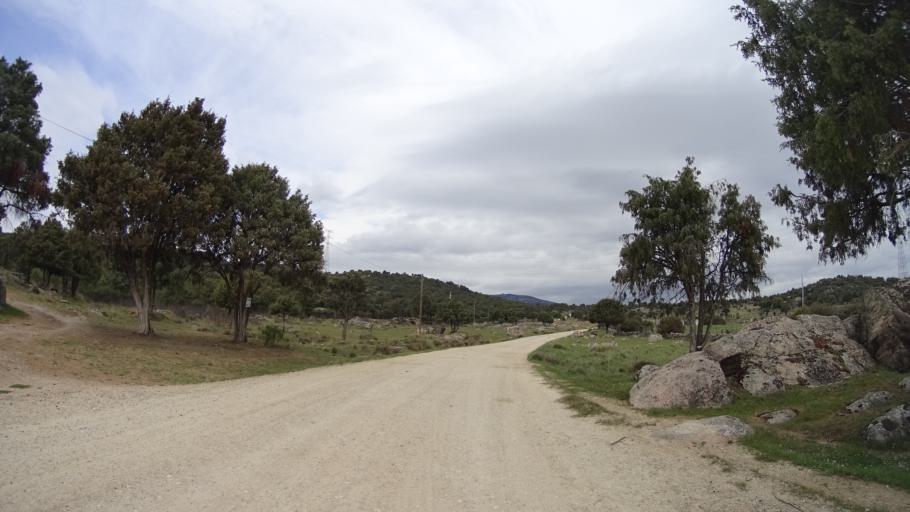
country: ES
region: Madrid
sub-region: Provincia de Madrid
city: Hoyo de Manzanares
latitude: 40.6113
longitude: -3.8780
